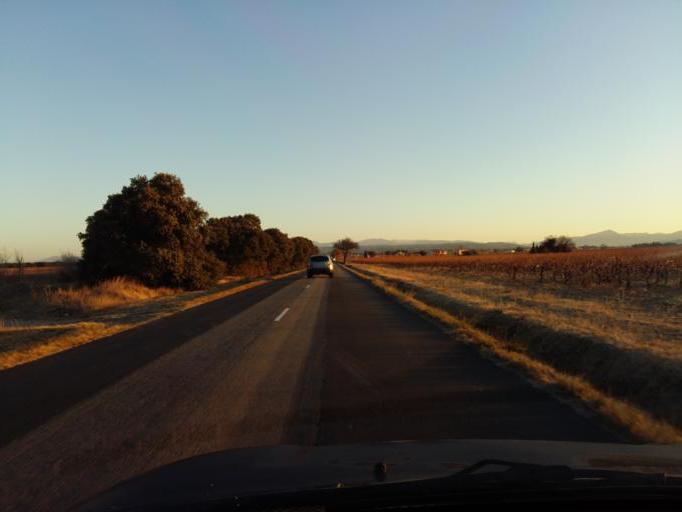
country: FR
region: Rhone-Alpes
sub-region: Departement de la Drome
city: Tulette
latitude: 44.2683
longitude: 4.9065
